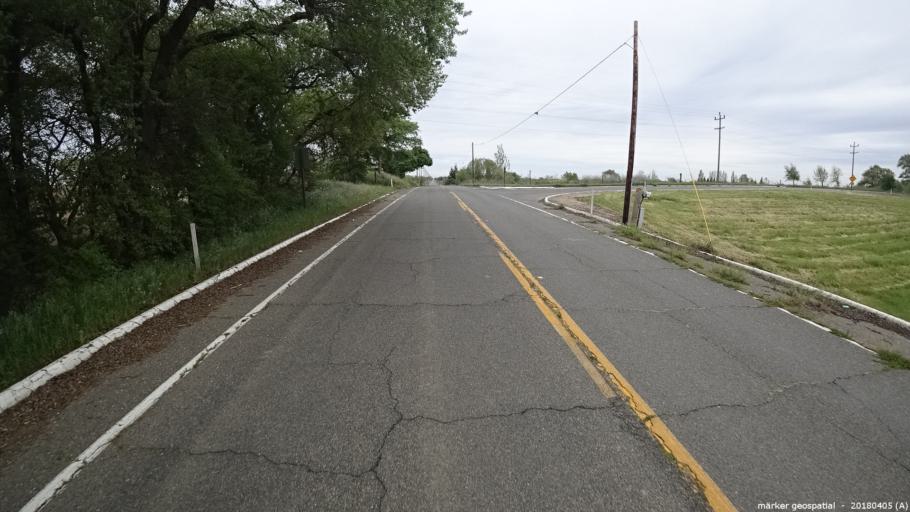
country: US
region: California
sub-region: Sacramento County
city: Walnut Grove
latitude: 38.3206
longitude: -121.5205
